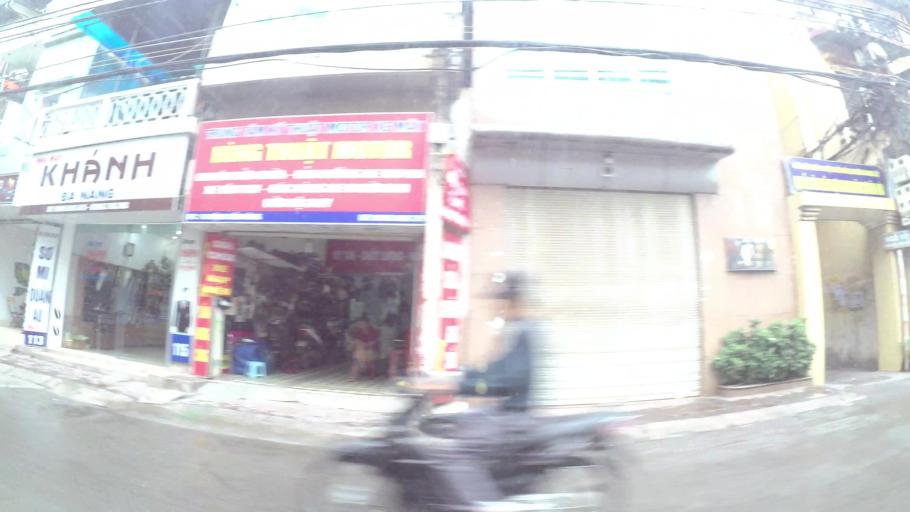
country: VN
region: Ha Noi
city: Dong Da
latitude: 21.0126
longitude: 105.8233
